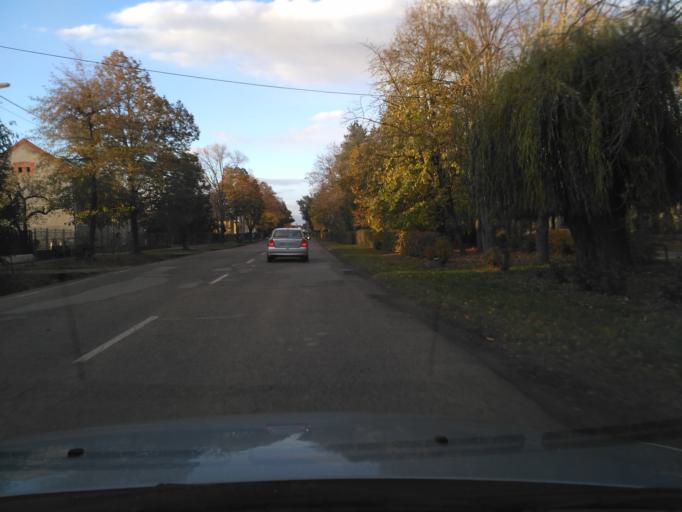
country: SK
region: Kosicky
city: Trebisov
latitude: 48.6470
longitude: 21.6796
